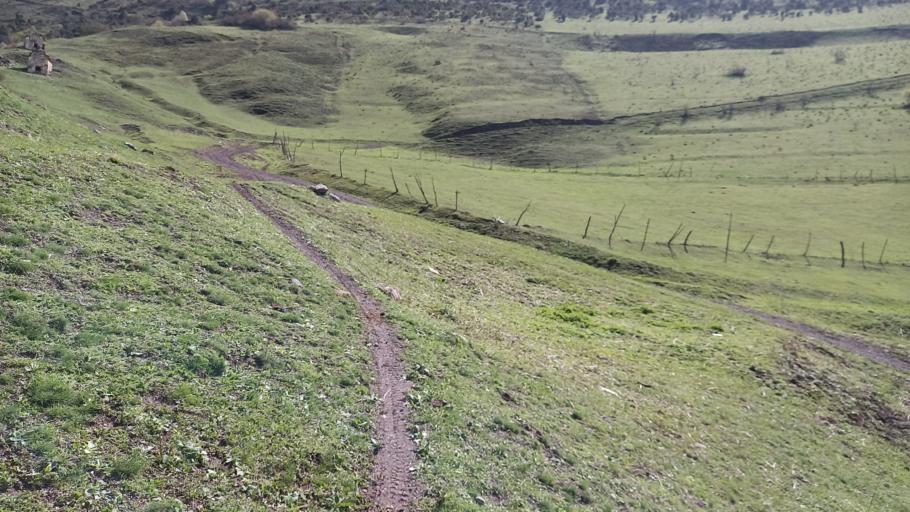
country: RU
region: Ingushetiya
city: Dzhayrakh
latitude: 42.8042
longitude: 44.7608
